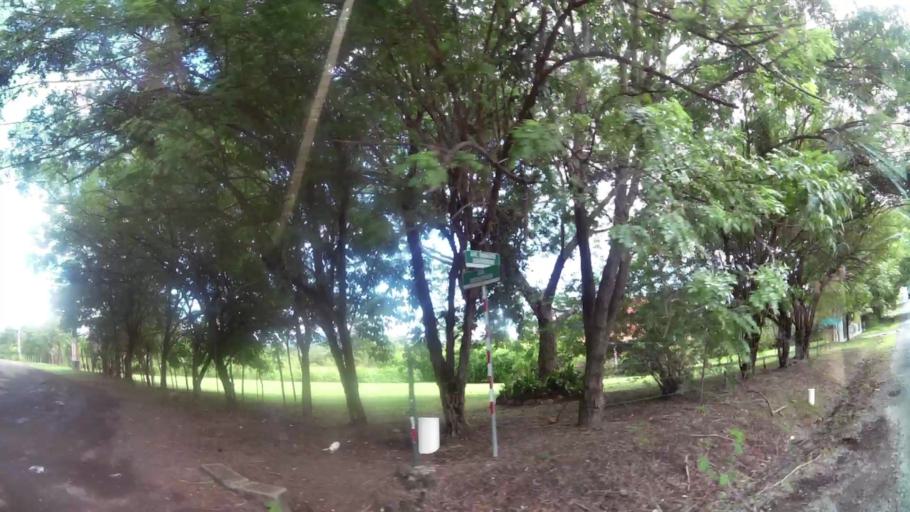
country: PA
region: Panama
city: Nueva Gorgona
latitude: 8.5359
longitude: -79.8988
